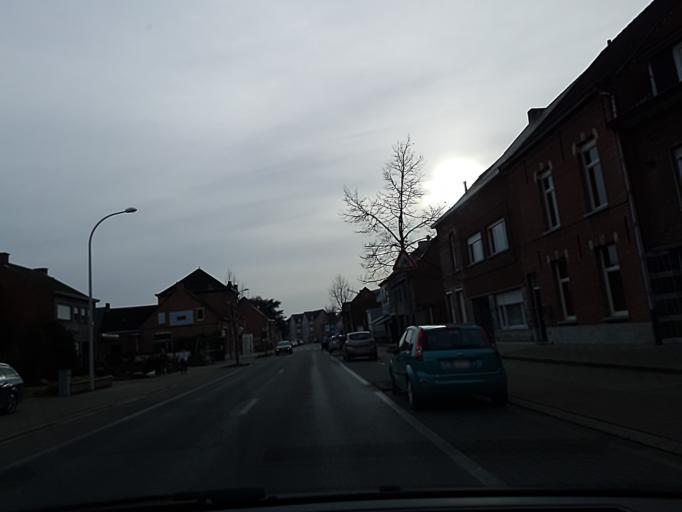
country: BE
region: Flanders
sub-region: Provincie Antwerpen
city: Lier
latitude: 51.0990
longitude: 4.6074
